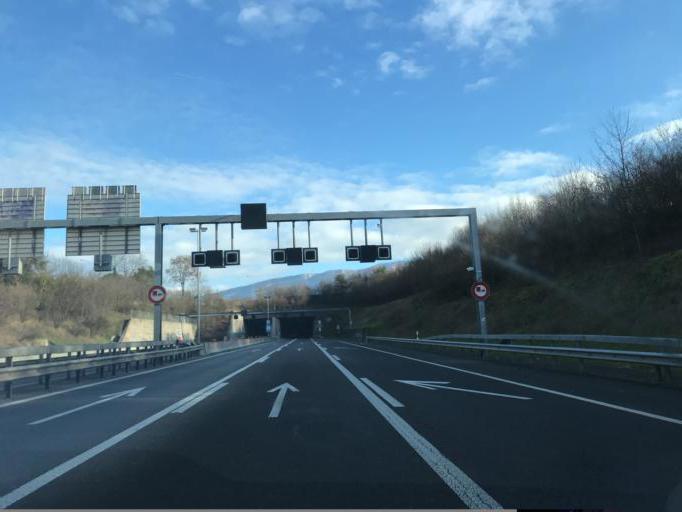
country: CH
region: Geneva
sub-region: Geneva
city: Plan-les-Ouates
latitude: 46.1630
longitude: 6.1041
